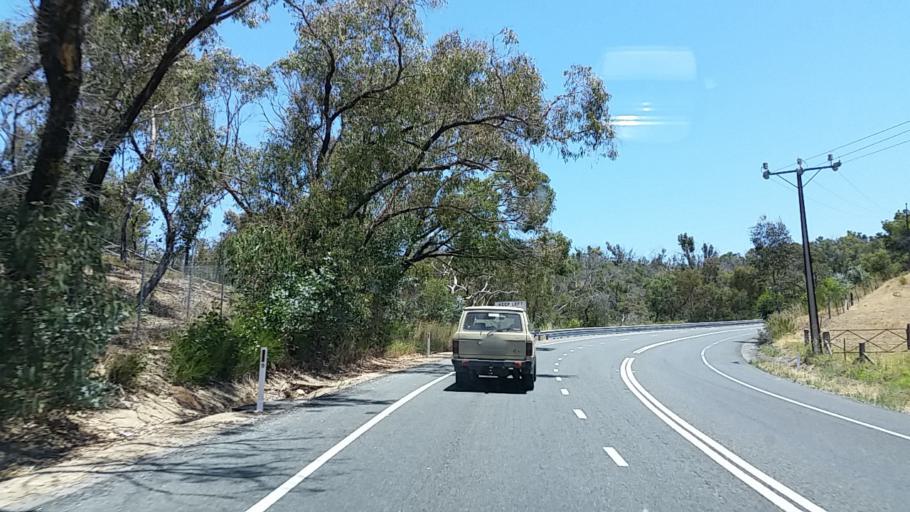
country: AU
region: South Australia
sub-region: Tea Tree Gully
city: Golden Grove
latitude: -34.8189
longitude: 138.7985
